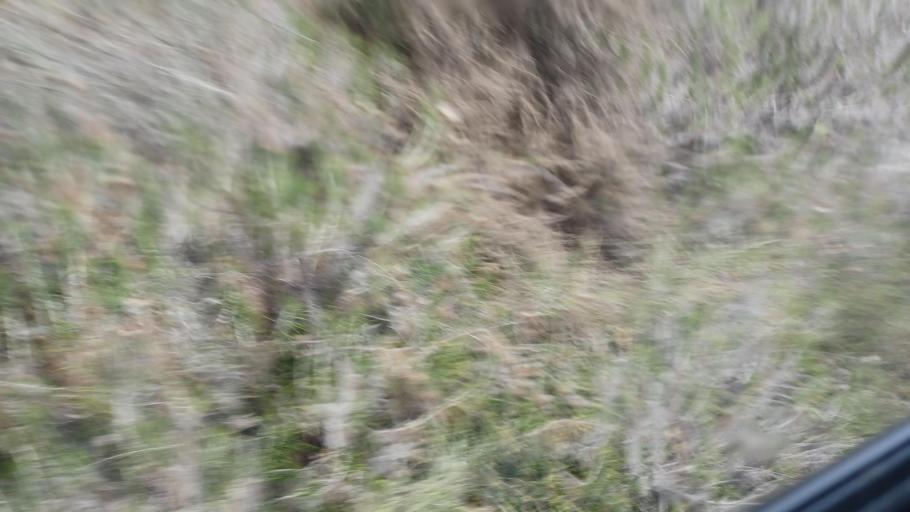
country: CY
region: Pafos
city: Tala
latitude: 34.8774
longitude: 32.4559
